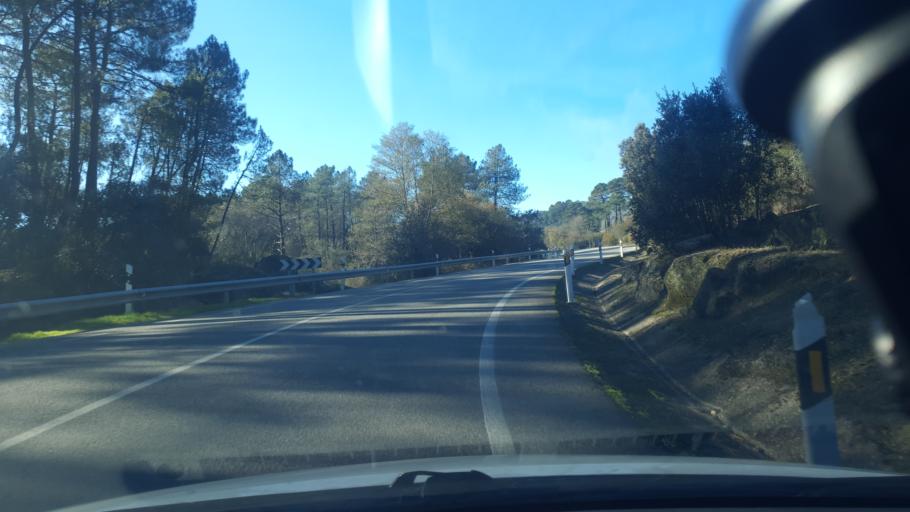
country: ES
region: Castille and Leon
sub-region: Provincia de Avila
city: Mombeltran
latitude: 40.2200
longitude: -5.0361
